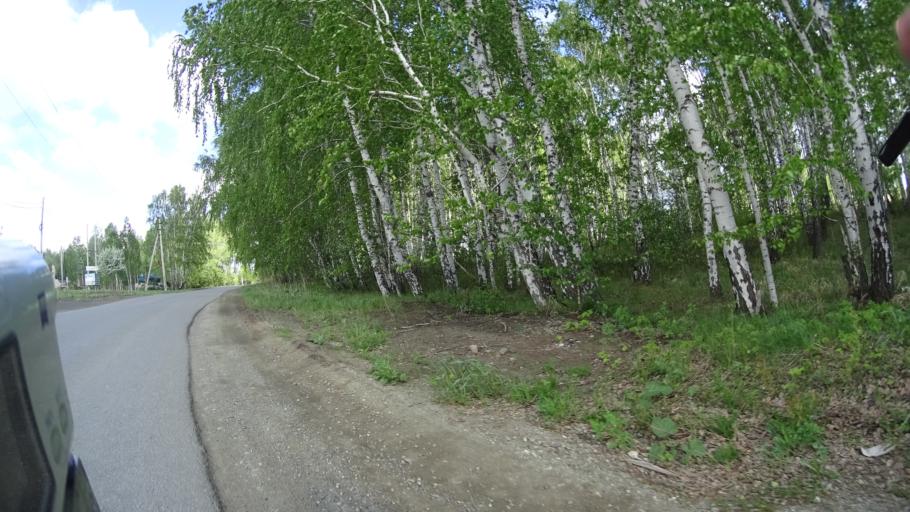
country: RU
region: Chelyabinsk
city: Sargazy
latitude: 55.1616
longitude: 61.2440
